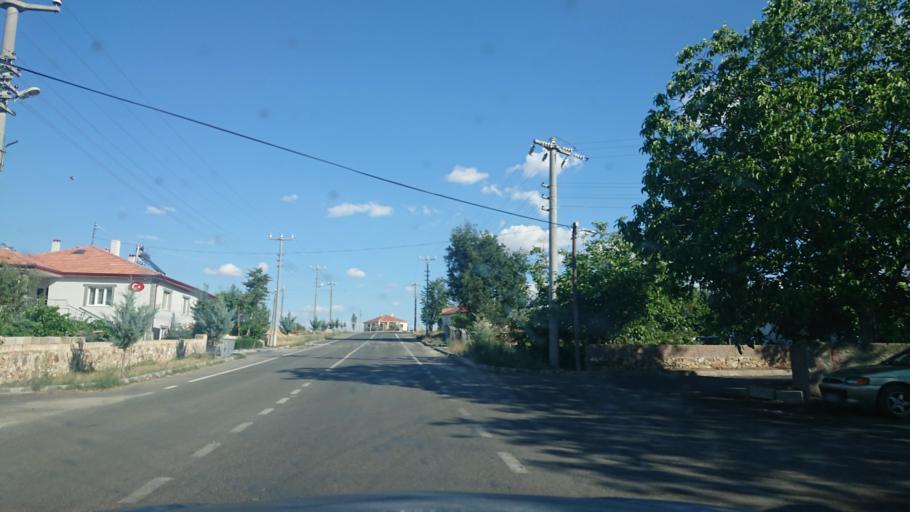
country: TR
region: Aksaray
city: Sariyahsi
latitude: 38.9868
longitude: 33.8525
